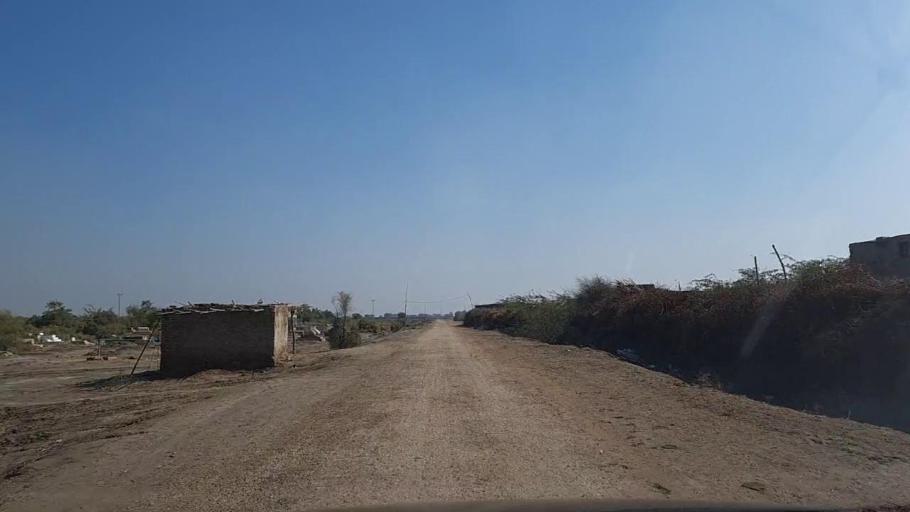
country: PK
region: Sindh
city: Nawabshah
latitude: 26.3189
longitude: 68.3456
